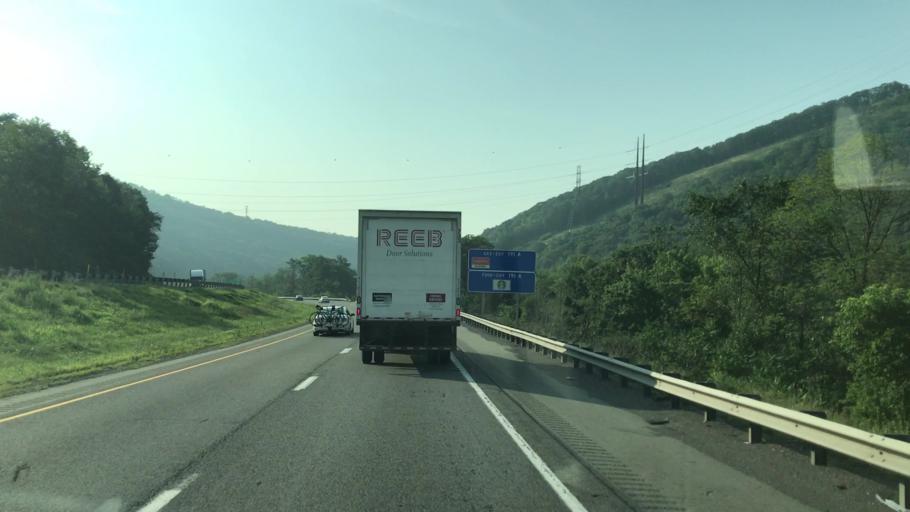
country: US
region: Pennsylvania
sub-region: Lackawanna County
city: Chinchilla
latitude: 41.4720
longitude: -75.6775
